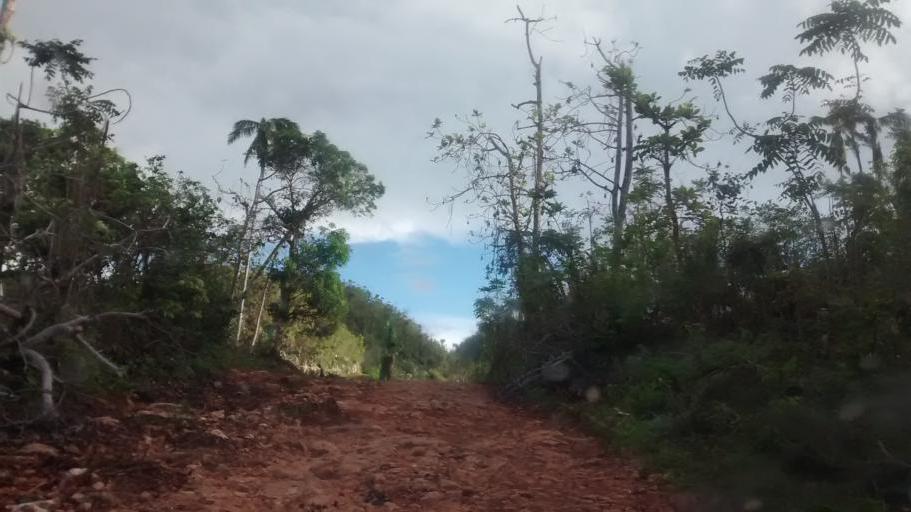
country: HT
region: Grandans
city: Corail
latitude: 18.5120
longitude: -73.7835
